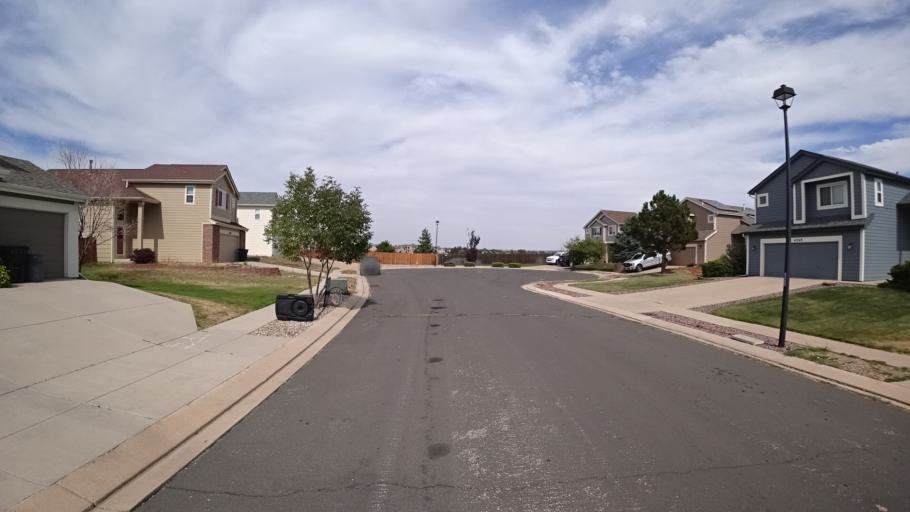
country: US
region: Colorado
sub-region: El Paso County
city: Cimarron Hills
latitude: 38.9055
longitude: -104.7146
